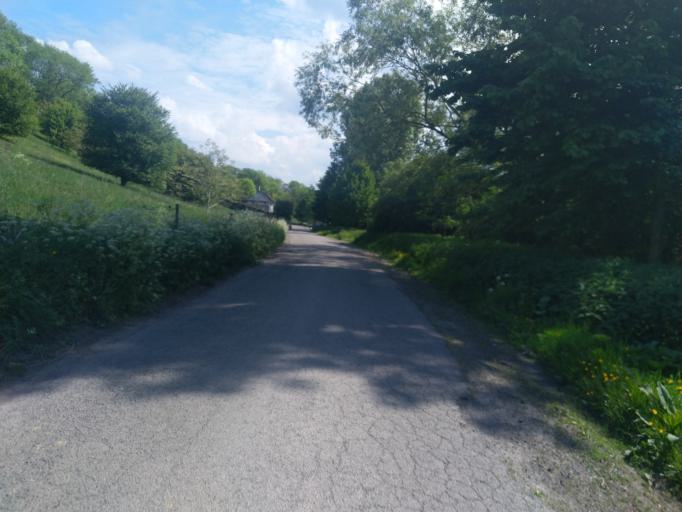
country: BE
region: Wallonia
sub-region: Province du Hainaut
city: Chasse Royale
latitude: 50.4164
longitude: 3.9695
